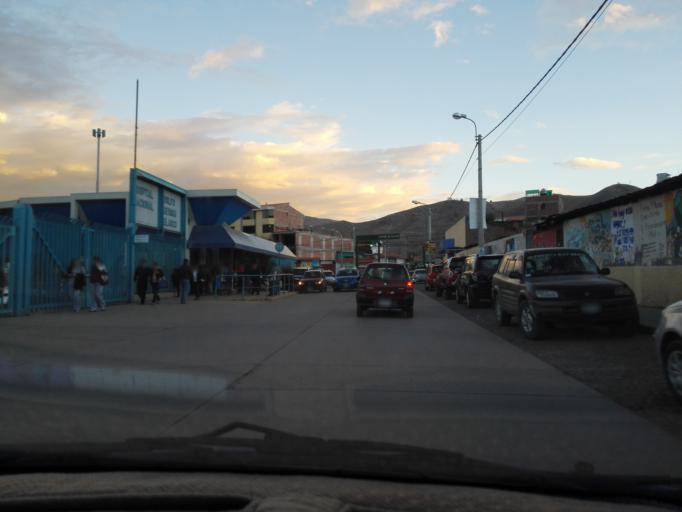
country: PE
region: Cusco
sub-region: Provincia de Cusco
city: Cusco
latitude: -13.5249
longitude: -71.9612
